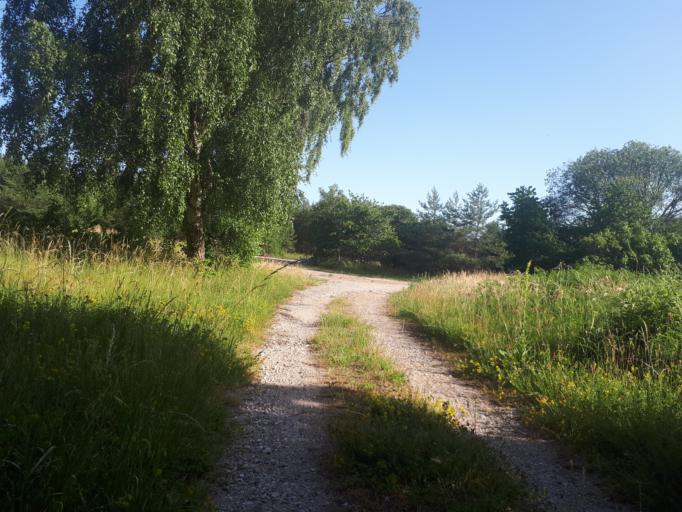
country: SE
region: Gotland
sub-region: Gotland
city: Visby
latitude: 57.6077
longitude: 18.2863
